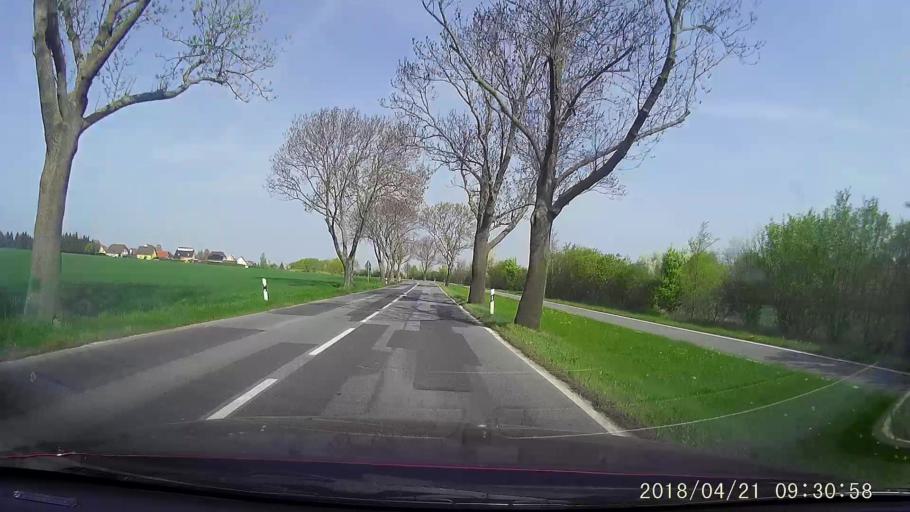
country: DE
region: Saxony
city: Radibor
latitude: 51.2067
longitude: 14.4009
